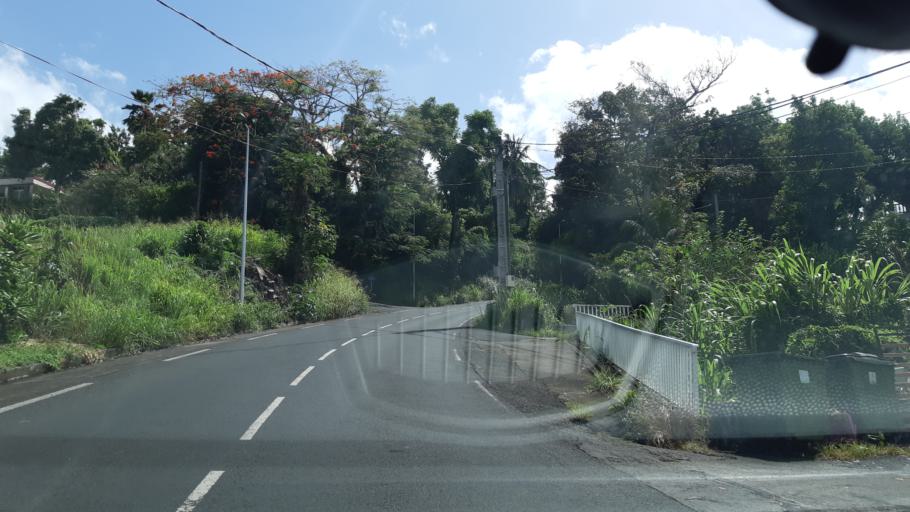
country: GP
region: Guadeloupe
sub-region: Guadeloupe
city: Basse-Terre
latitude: 16.0028
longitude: -61.7165
